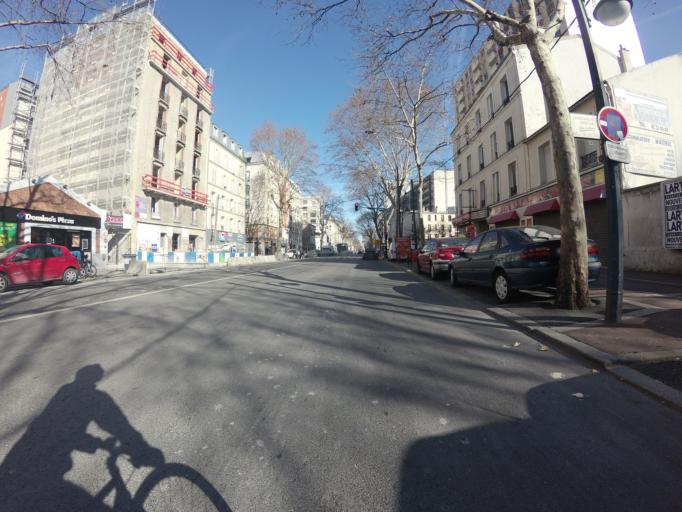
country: FR
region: Ile-de-France
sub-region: Departement des Hauts-de-Seine
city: Clichy
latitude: 48.8990
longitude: 2.3130
